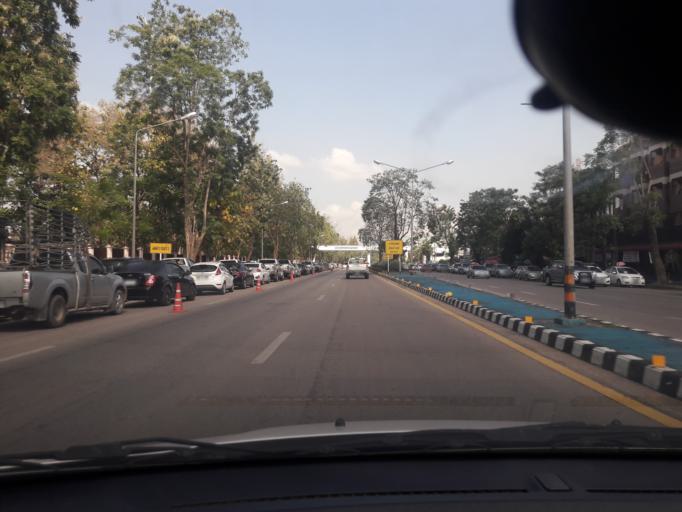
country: TH
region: Lampang
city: Lampang
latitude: 18.2340
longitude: 99.4905
